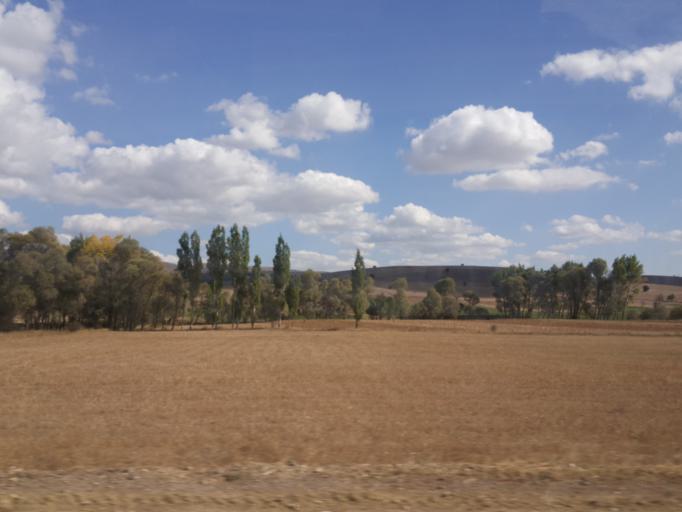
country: TR
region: Tokat
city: Camlibel
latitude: 40.1924
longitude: 36.4580
